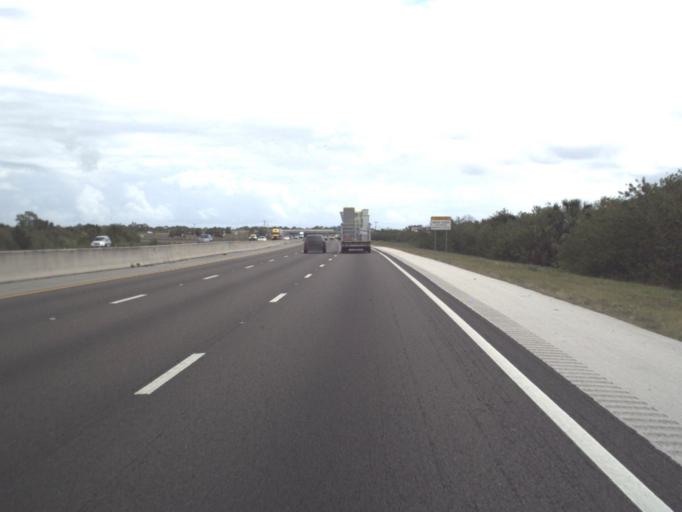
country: US
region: Florida
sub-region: Brevard County
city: Rockledge
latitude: 28.2968
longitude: -80.7503
